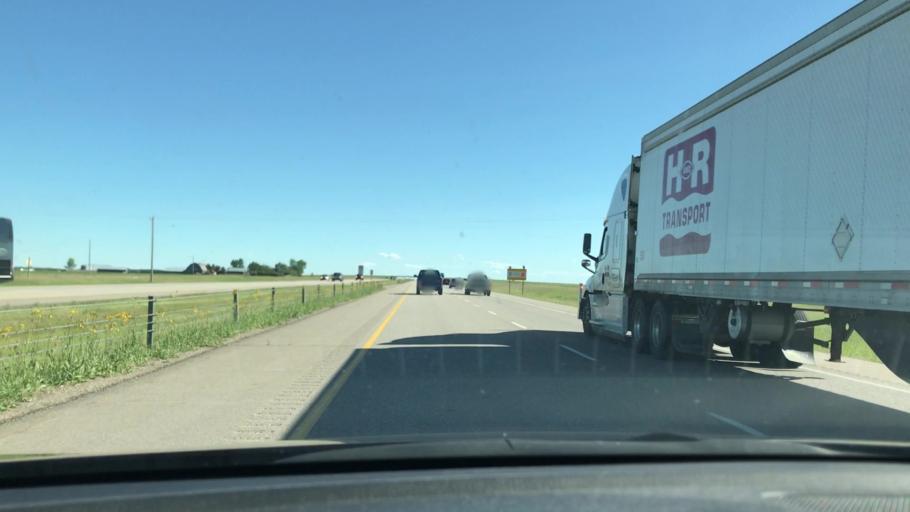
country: CA
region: Alberta
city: Didsbury
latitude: 51.6798
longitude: -114.0256
